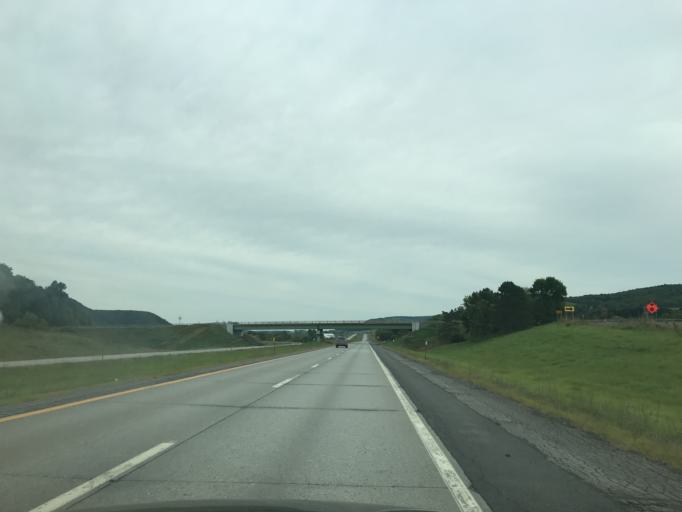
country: US
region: New York
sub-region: Schoharie County
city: Cobleskill
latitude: 42.6399
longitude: -74.5494
